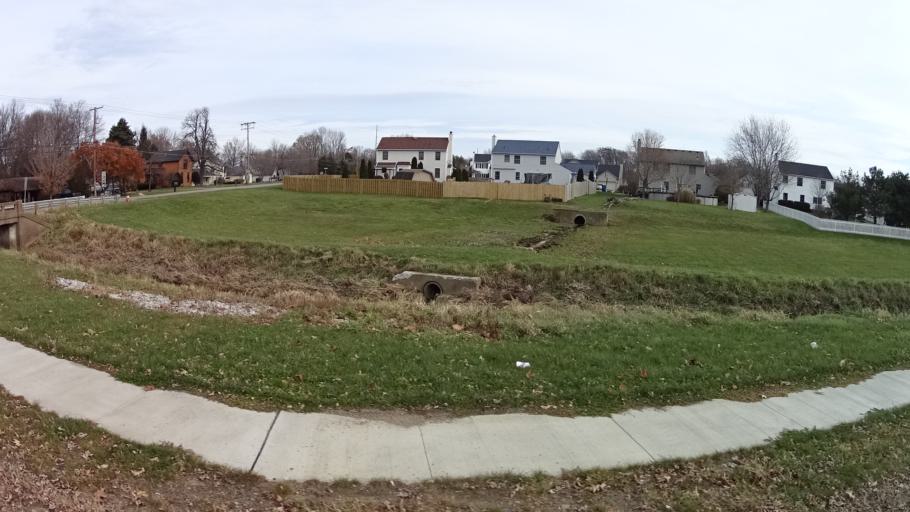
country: US
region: Ohio
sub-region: Lorain County
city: North Ridgeville
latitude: 41.3736
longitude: -82.0019
